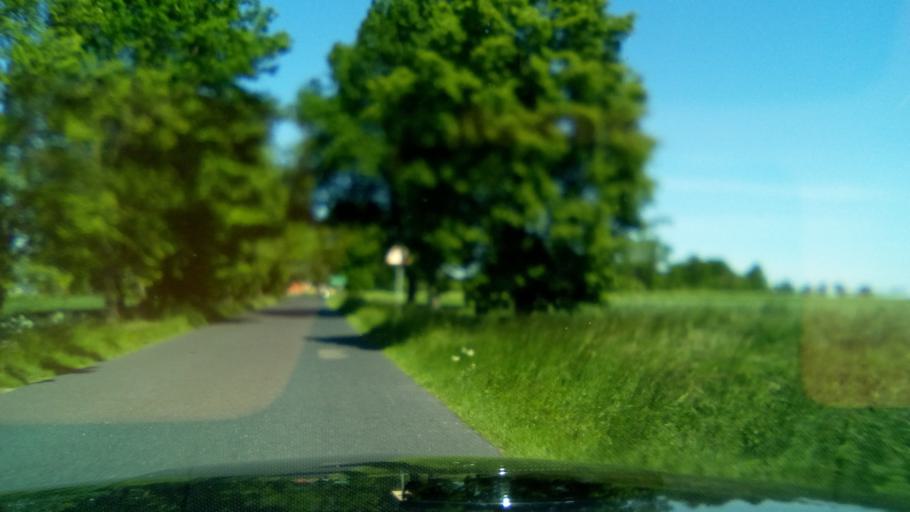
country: PL
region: Greater Poland Voivodeship
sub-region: Powiat gnieznienski
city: Niechanowo
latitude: 52.4605
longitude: 17.6620
